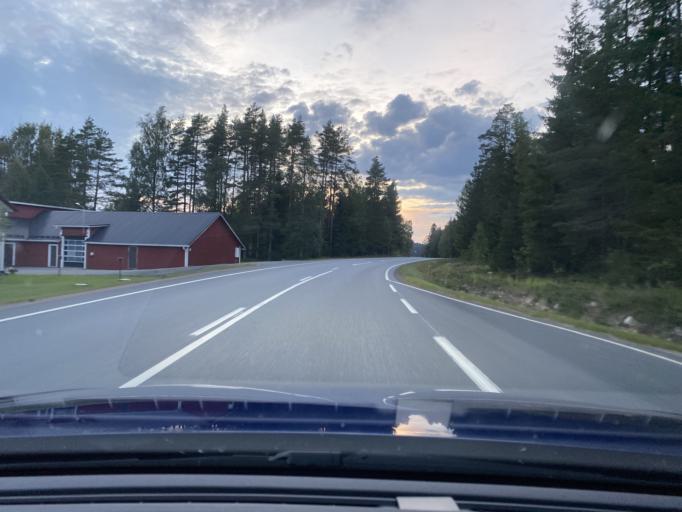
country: FI
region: Satakunta
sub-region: Pohjois-Satakunta
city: Honkajoki
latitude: 62.2190
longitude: 22.2862
